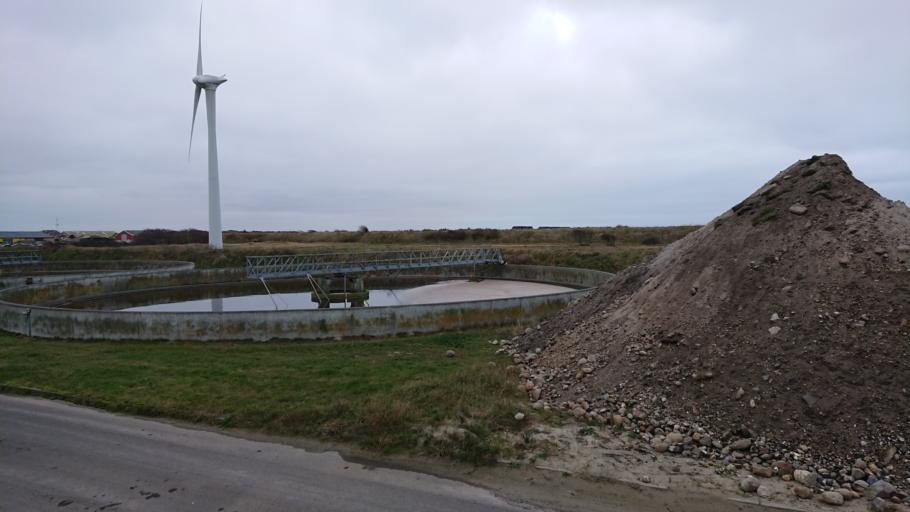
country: DK
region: North Denmark
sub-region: Frederikshavn Kommune
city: Skagen
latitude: 57.7388
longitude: 10.5677
